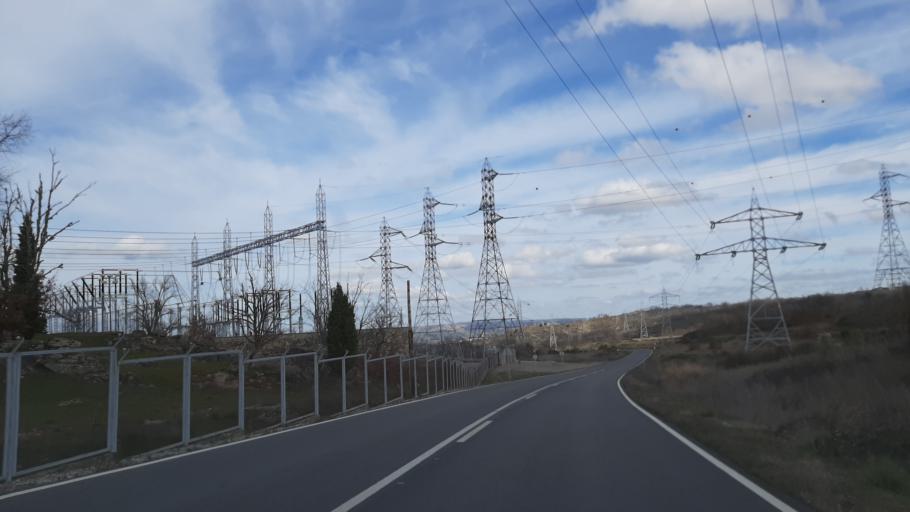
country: ES
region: Castille and Leon
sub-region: Provincia de Salamanca
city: Villarino de los Aires
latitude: 41.2542
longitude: -6.4867
